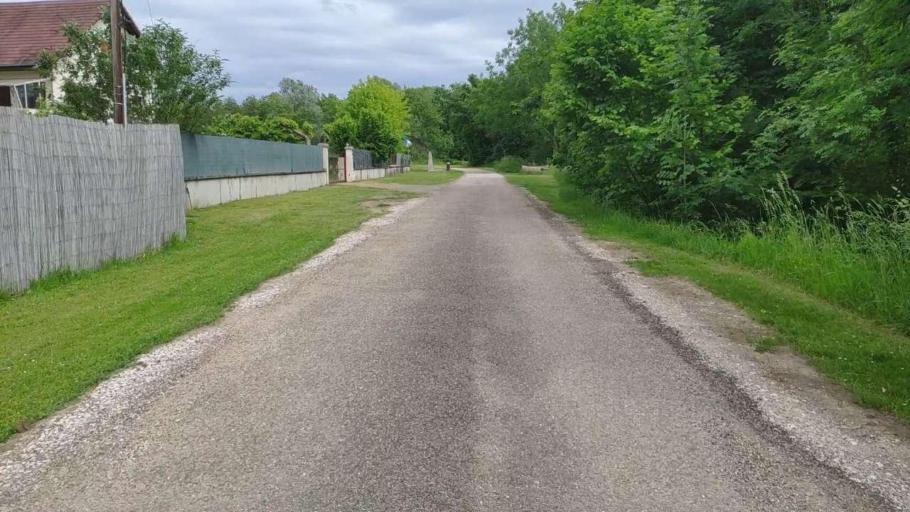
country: FR
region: Franche-Comte
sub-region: Departement du Jura
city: Perrigny
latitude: 46.7748
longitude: 5.5728
